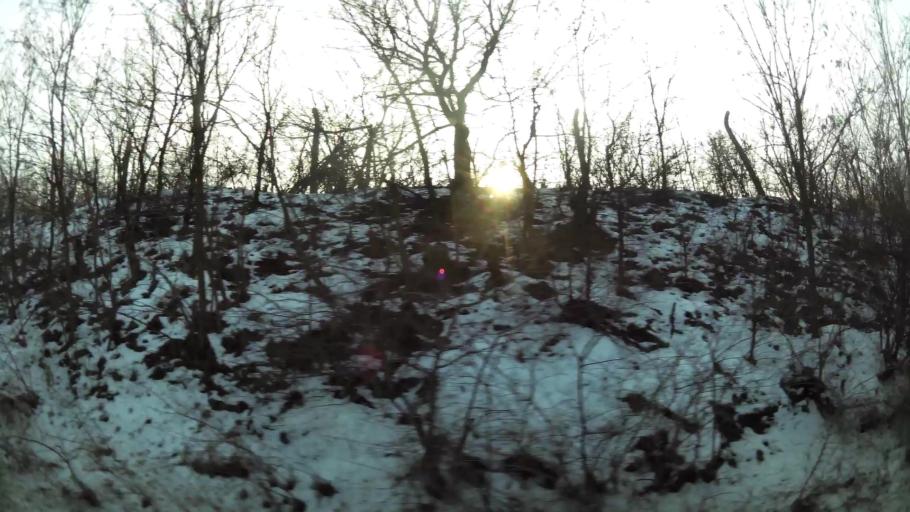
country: MK
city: Miladinovci
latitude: 41.9765
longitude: 21.6302
